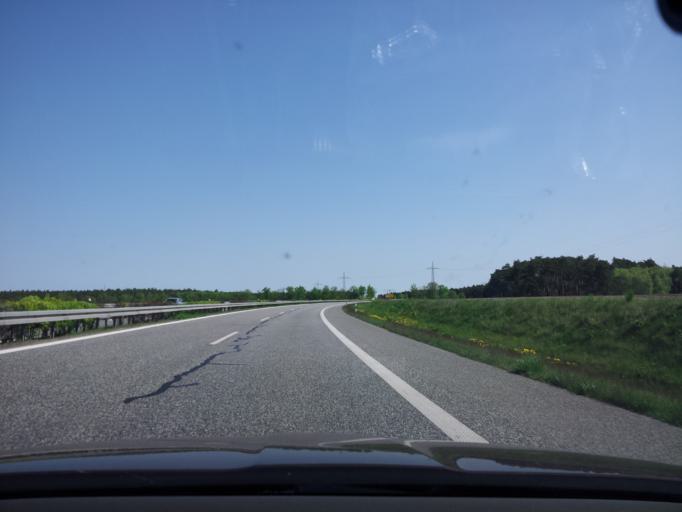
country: DE
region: Brandenburg
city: Ludwigsfelde
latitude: 52.2747
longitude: 13.2712
